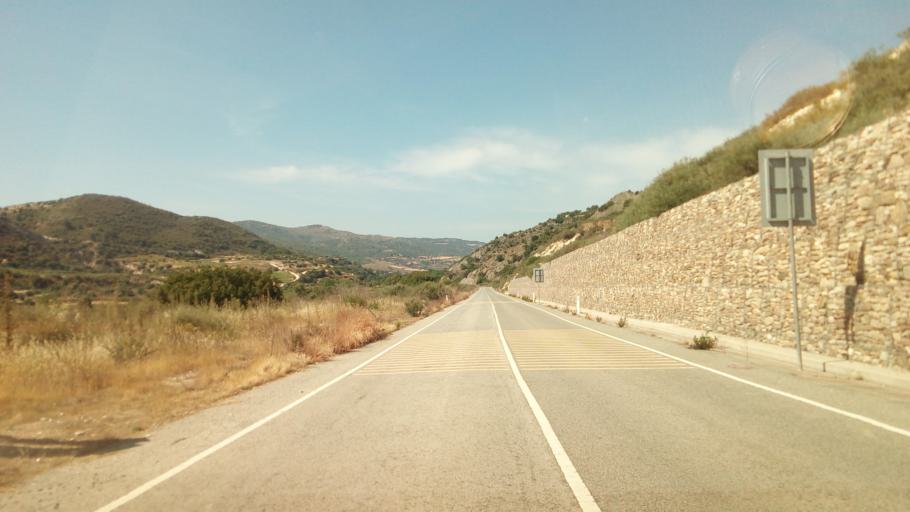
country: CY
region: Limassol
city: Pachna
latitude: 34.8062
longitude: 32.7119
